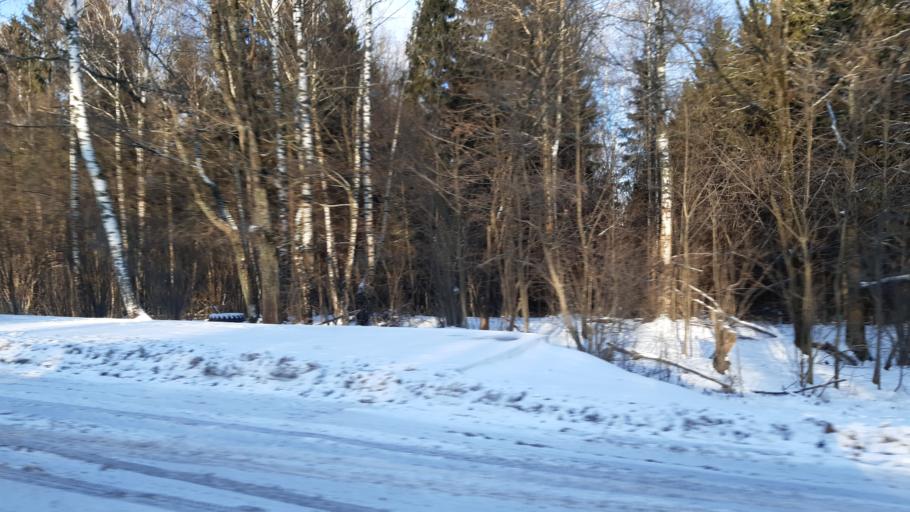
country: RU
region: Moskovskaya
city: Svatkovo
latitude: 56.3005
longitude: 38.3500
